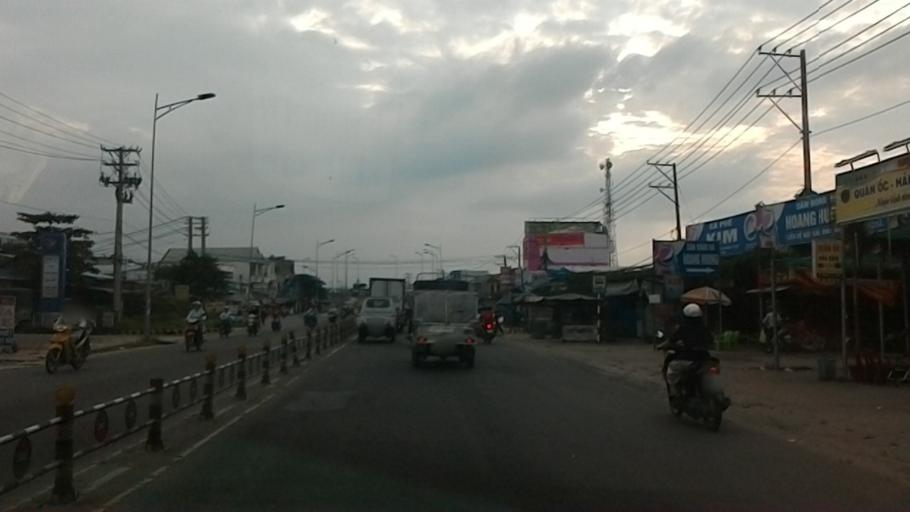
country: VN
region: Can Tho
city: Cai Rang
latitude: 10.0106
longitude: 105.7515
